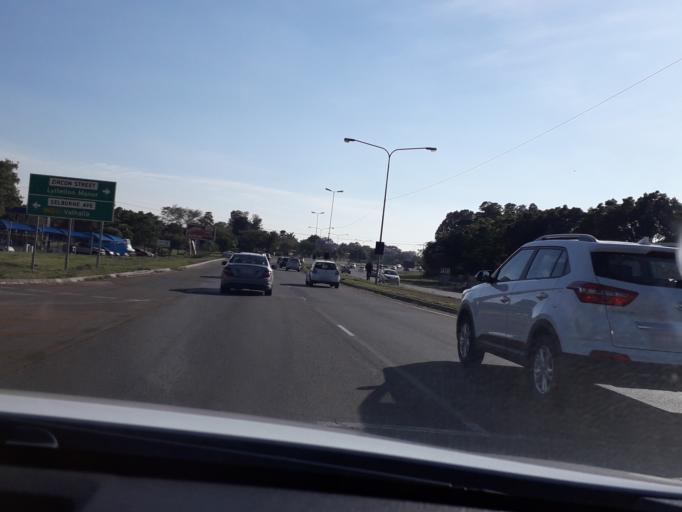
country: ZA
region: Gauteng
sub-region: City of Tshwane Metropolitan Municipality
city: Centurion
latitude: -25.8208
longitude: 28.1946
